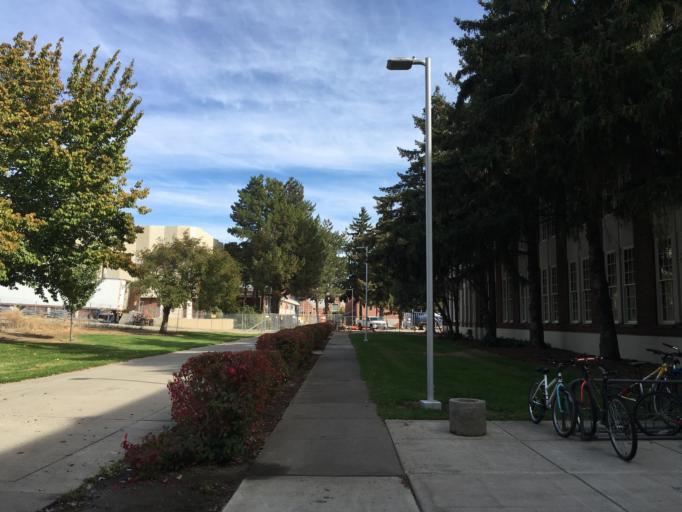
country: US
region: Washington
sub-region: Kittitas County
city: Ellensburg
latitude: 47.0018
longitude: -120.5427
